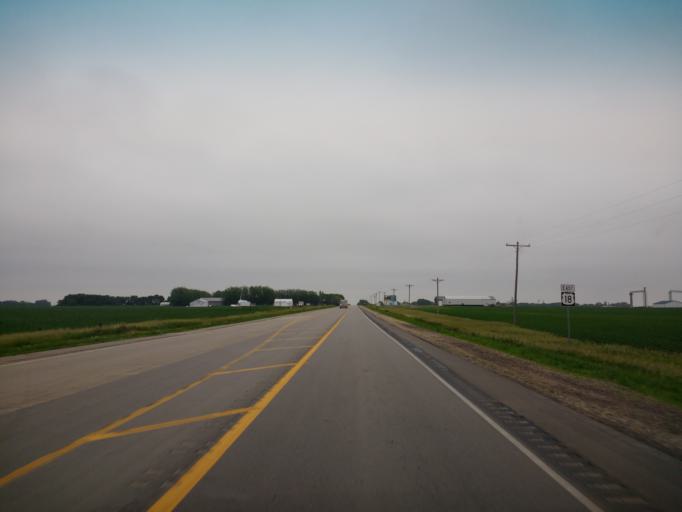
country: US
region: Iowa
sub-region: O'Brien County
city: Hartley
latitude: 43.1850
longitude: -95.5049
